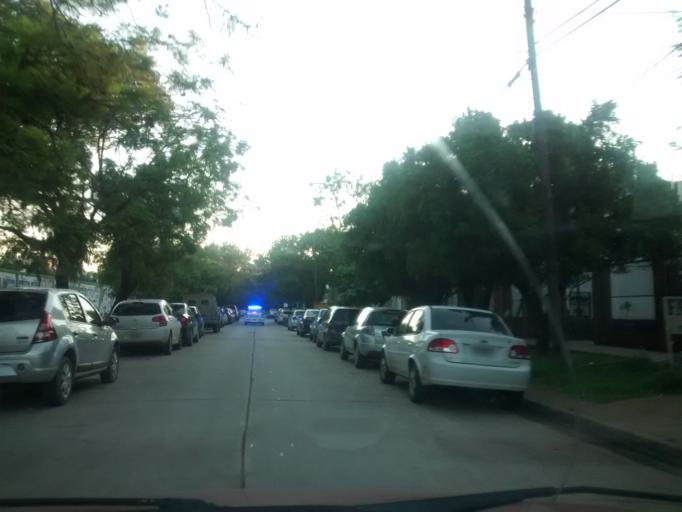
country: AR
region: Chaco
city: Resistencia
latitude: -27.4444
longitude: -58.9841
